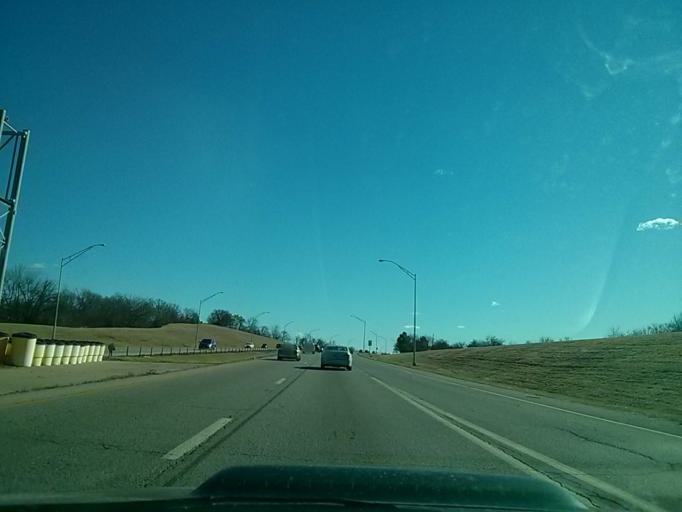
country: US
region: Oklahoma
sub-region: Tulsa County
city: Tulsa
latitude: 36.1018
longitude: -96.0083
